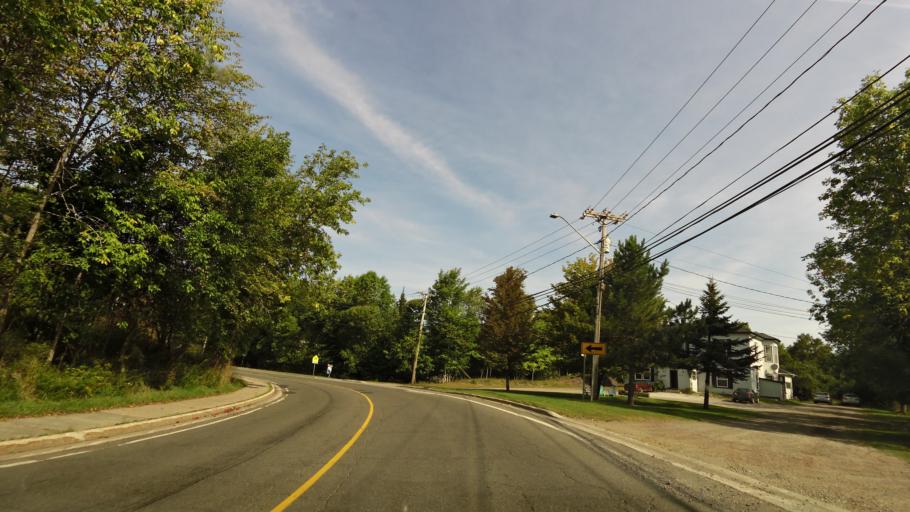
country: CA
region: New Brunswick
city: Hampton
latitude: 45.5361
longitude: -65.8306
